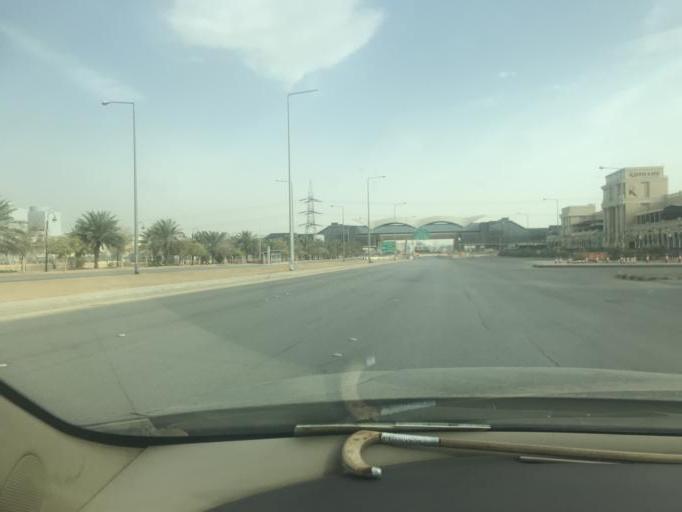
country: SA
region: Ar Riyad
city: Riyadh
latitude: 24.8046
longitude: 46.6943
